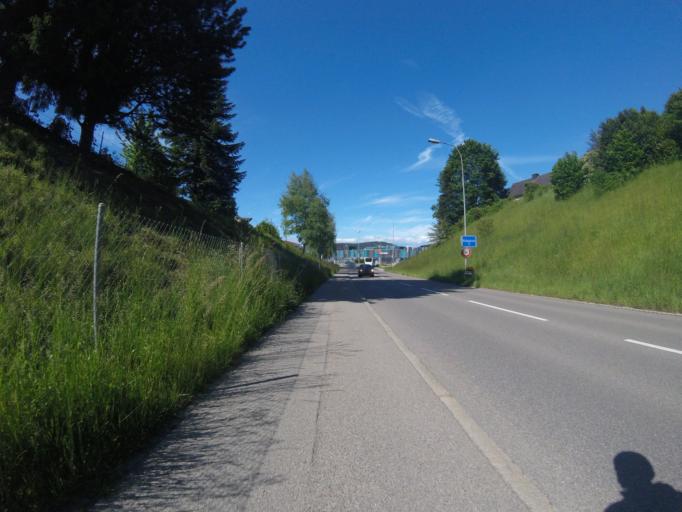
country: CH
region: Saint Gallen
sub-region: Wahlkreis Wil
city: Wil
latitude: 47.4443
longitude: 9.0507
